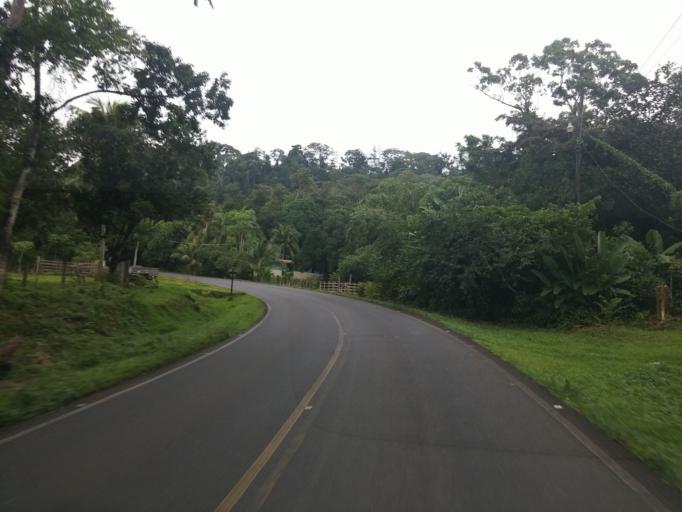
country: CR
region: Alajuela
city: Bijagua
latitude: 10.8095
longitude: -85.0231
